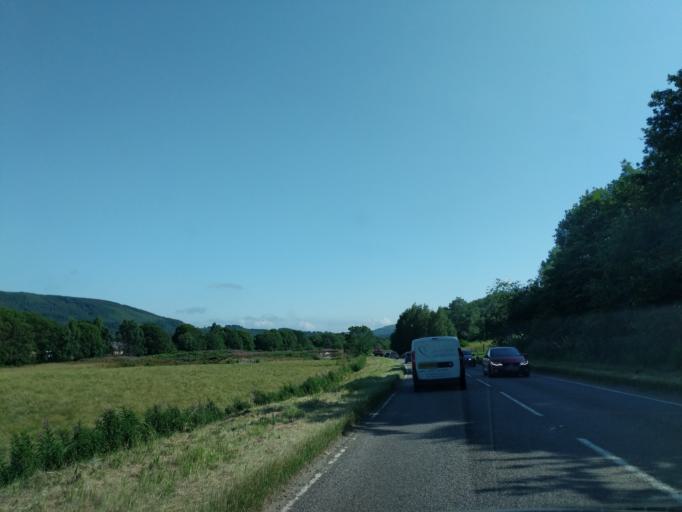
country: GB
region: Scotland
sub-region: Moray
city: Rothes
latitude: 57.5161
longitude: -3.2081
